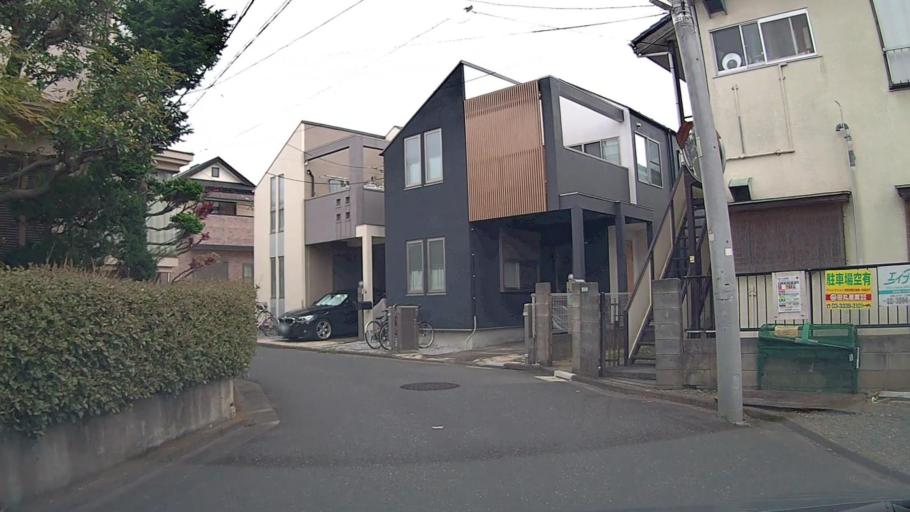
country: JP
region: Tokyo
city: Musashino
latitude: 35.7303
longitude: 139.6017
